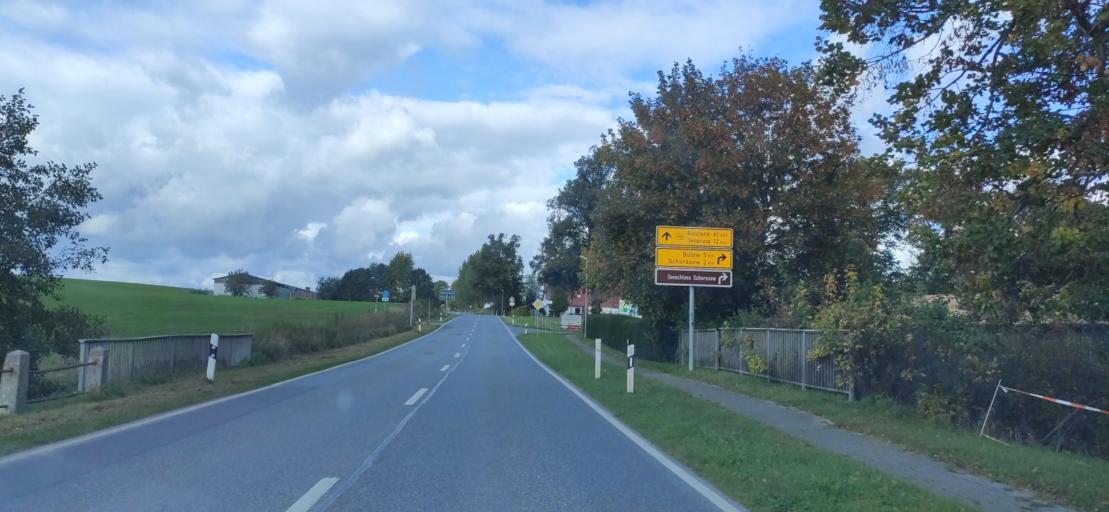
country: DE
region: Mecklenburg-Vorpommern
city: Gross Wokern
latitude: 53.6716
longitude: 12.5435
